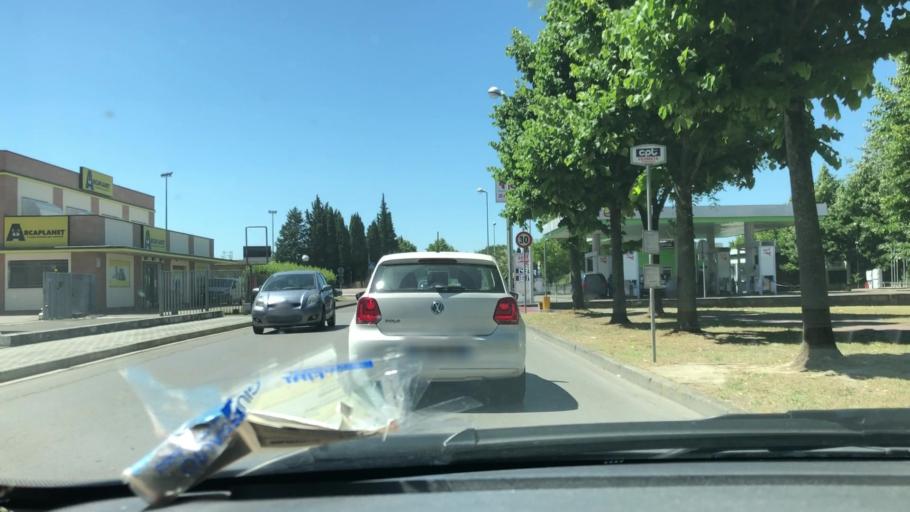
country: IT
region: Tuscany
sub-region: Province of Pisa
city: Pontedera
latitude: 43.6553
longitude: 10.6316
